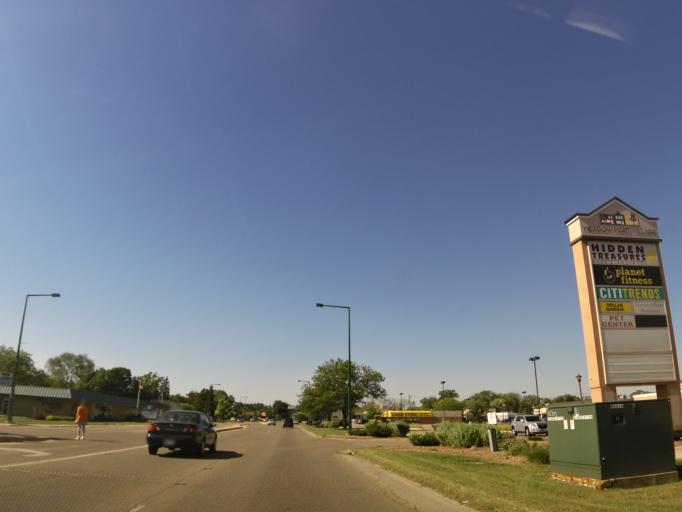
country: US
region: Illinois
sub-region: Winnebago County
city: Loves Park
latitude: 42.3228
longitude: -89.0579
